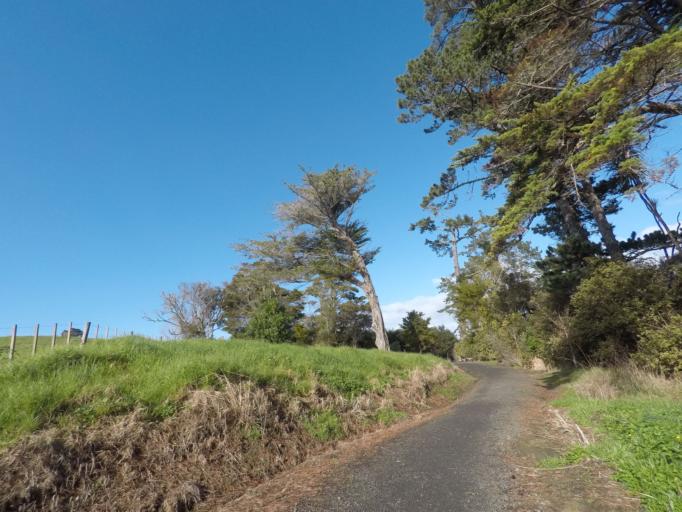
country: NZ
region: Auckland
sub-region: Auckland
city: Warkworth
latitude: -36.4308
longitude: 174.7184
